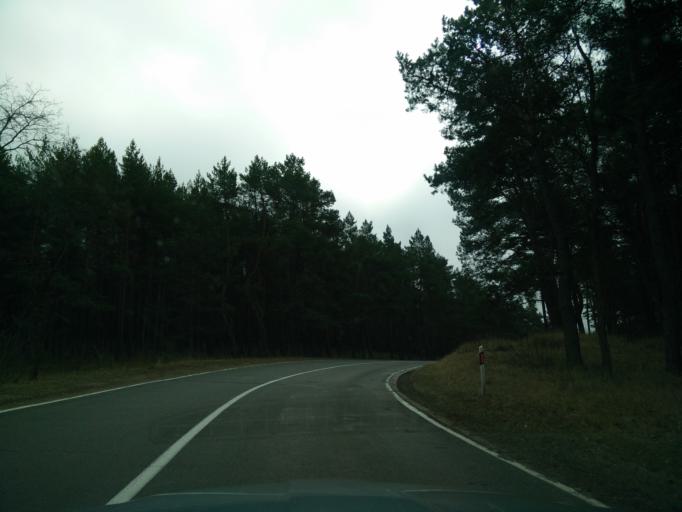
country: LT
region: Klaipedos apskritis
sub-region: Klaipeda
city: Klaipeda
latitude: 55.6639
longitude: 21.1162
